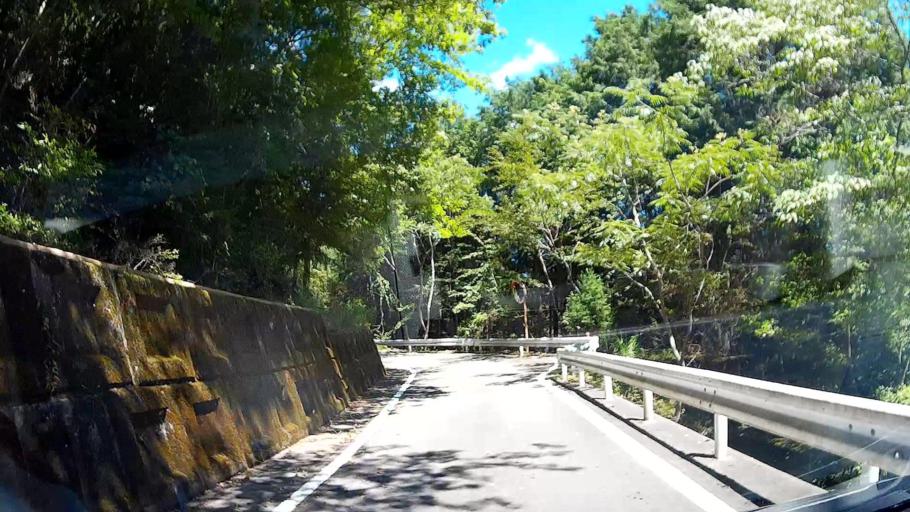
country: JP
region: Shizuoka
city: Shizuoka-shi
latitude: 35.1875
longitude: 138.2642
